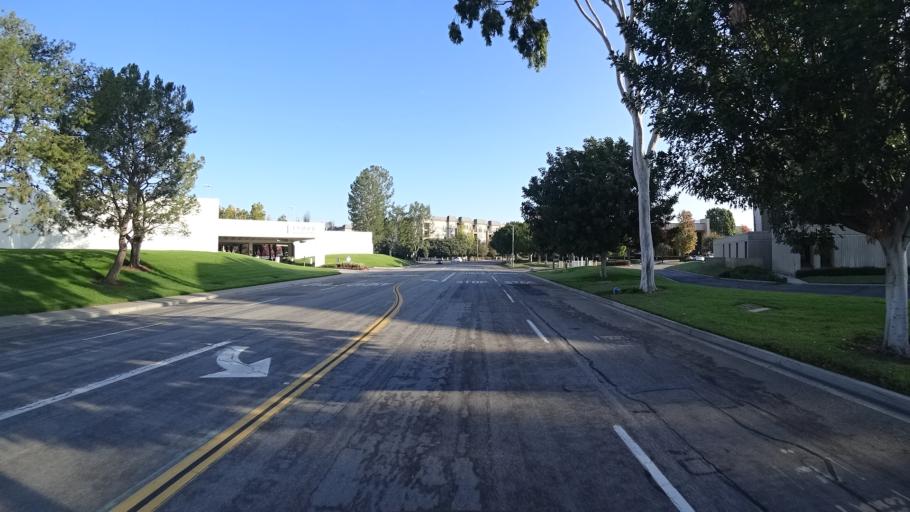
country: US
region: California
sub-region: Orange County
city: Irvine
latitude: 33.6718
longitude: -117.8618
